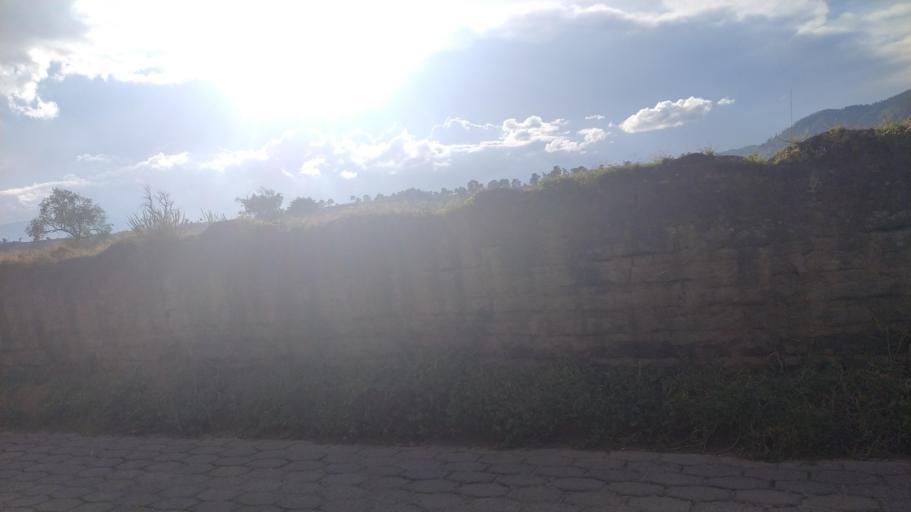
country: GT
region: Quetzaltenango
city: Salcaja
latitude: 14.8736
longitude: -91.4580
